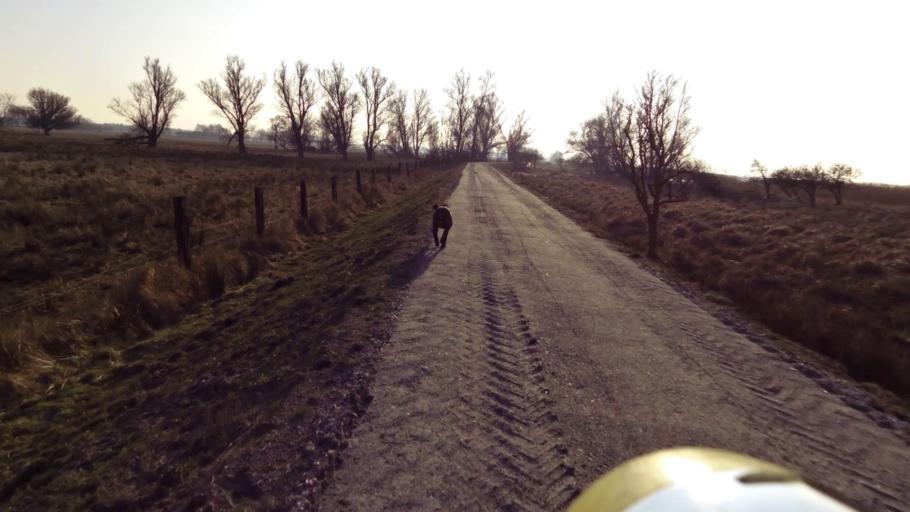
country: PL
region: West Pomeranian Voivodeship
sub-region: Powiat kamienski
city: Wolin
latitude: 53.7509
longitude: 14.5594
